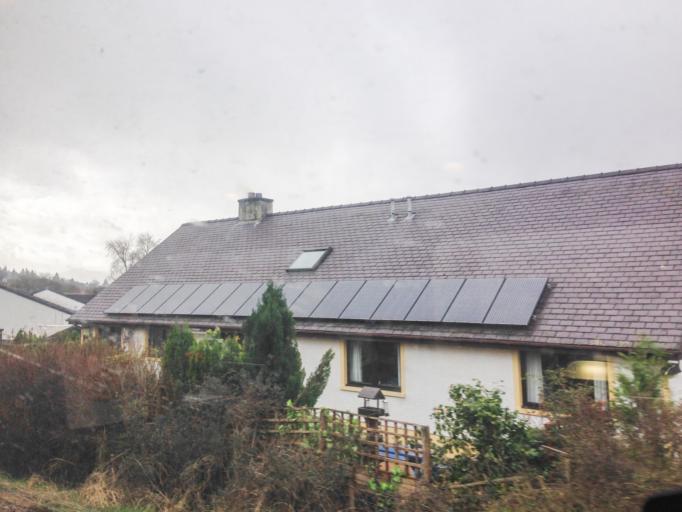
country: GB
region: Scotland
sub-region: Highland
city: Fort William
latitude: 56.8258
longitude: -5.0893
